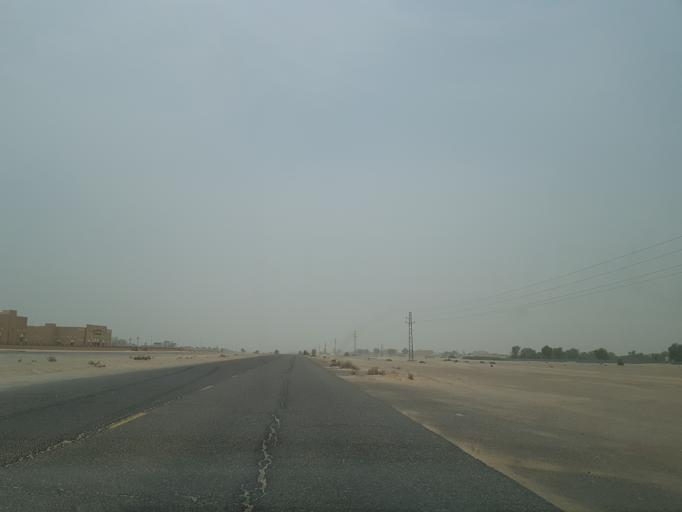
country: AE
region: Dubai
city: Dubai
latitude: 24.9354
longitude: 55.4719
